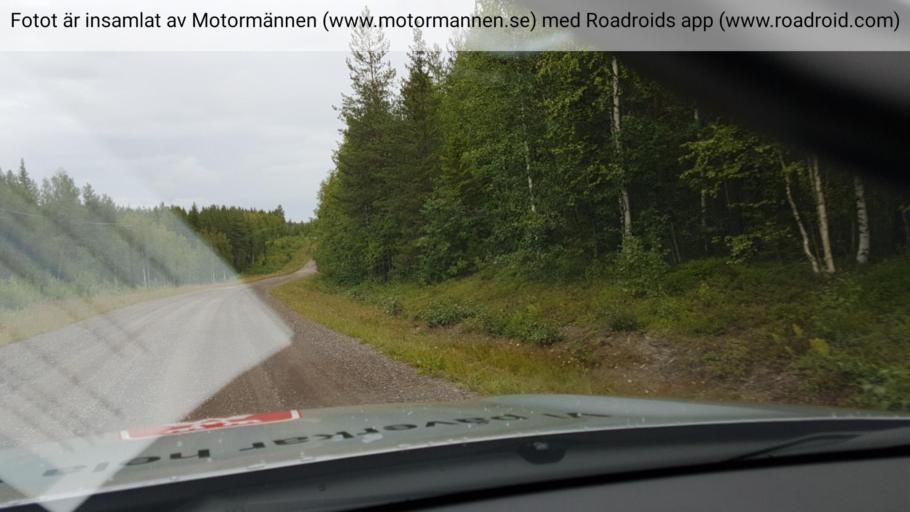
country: SE
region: Norrbotten
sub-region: Alvsbyns Kommun
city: AElvsbyn
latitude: 66.0340
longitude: 20.9924
